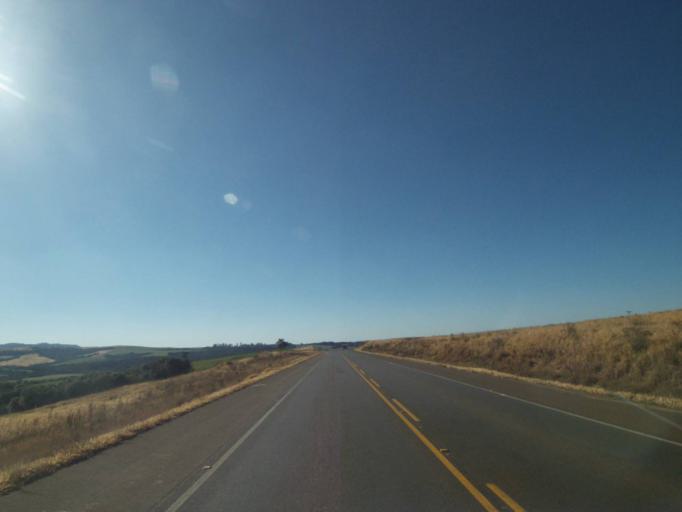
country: BR
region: Parana
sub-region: Tibagi
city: Tibagi
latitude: -24.6279
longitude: -50.4541
